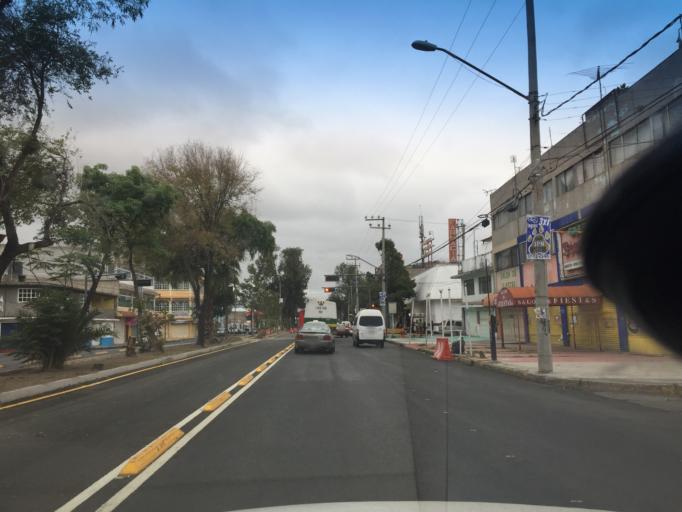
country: MX
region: Mexico City
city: Venustiano Carranza
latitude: 19.4716
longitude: -99.0671
